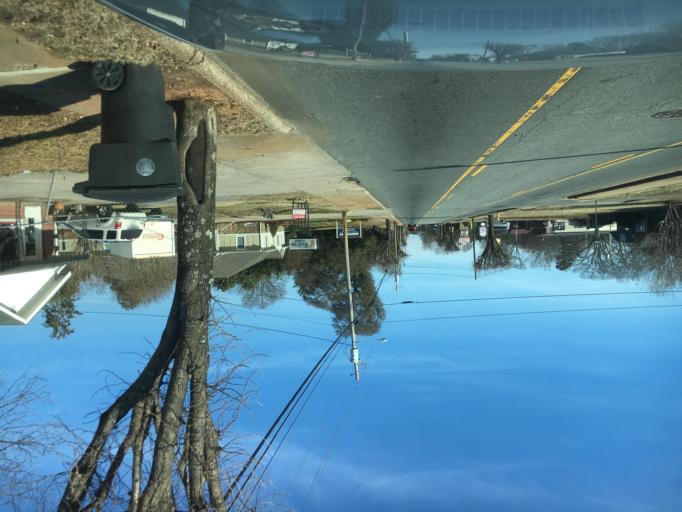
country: US
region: North Carolina
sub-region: Rutherford County
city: Forest City
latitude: 35.3189
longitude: -81.8582
